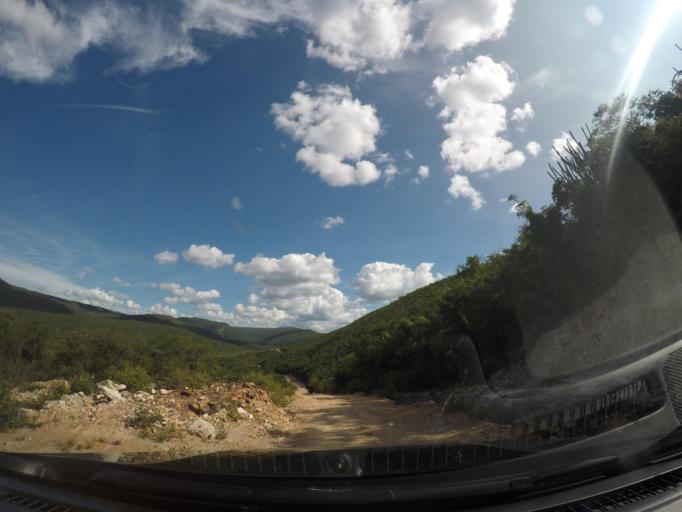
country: BR
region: Bahia
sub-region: Barra Da Estiva
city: Barra da Estiva
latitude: -13.2042
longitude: -41.5937
